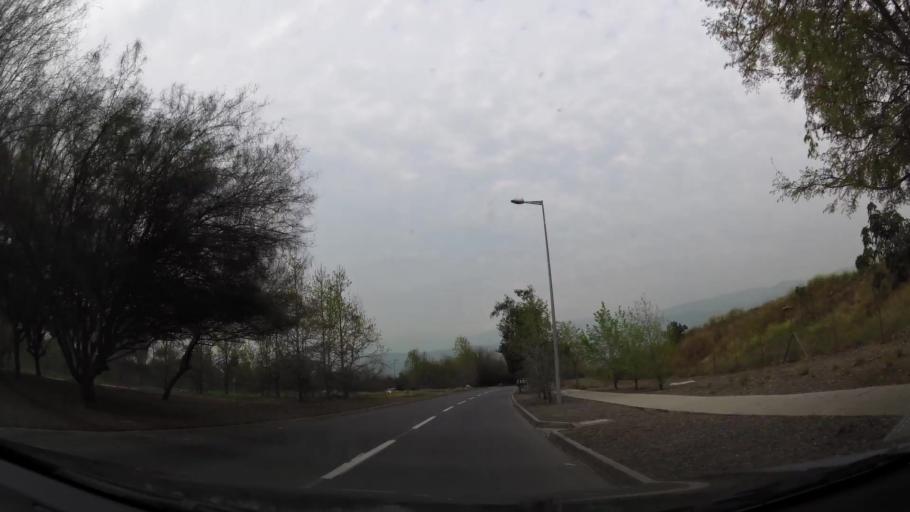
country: CL
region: Santiago Metropolitan
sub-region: Provincia de Chacabuco
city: Chicureo Abajo
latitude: -33.2796
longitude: -70.6325
